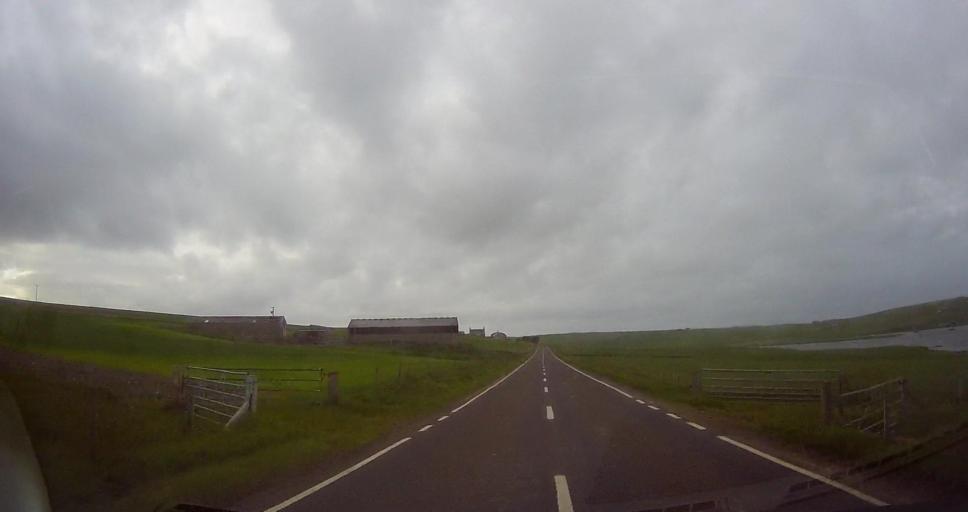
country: GB
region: Scotland
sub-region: Orkney Islands
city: Stromness
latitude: 59.0066
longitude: -3.2907
